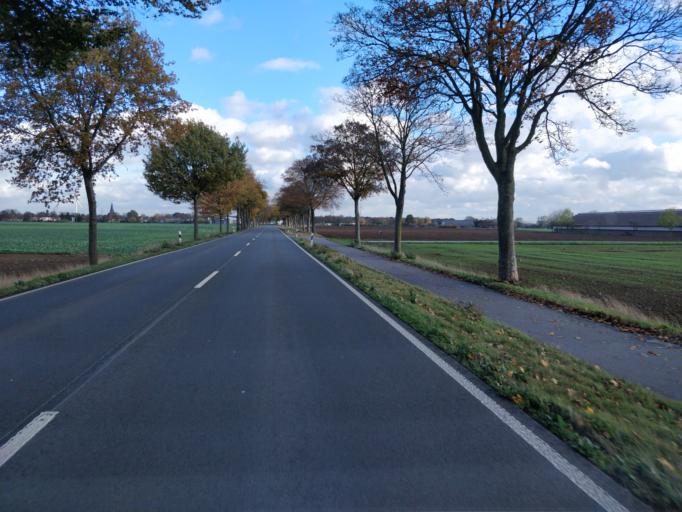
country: DE
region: North Rhine-Westphalia
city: Rees
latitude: 51.7747
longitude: 6.4418
